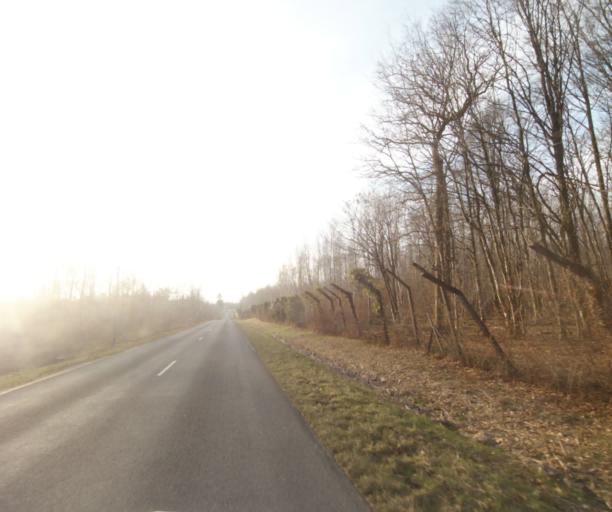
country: FR
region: Champagne-Ardenne
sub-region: Departement de la Haute-Marne
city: Chancenay
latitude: 48.6965
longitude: 4.9453
